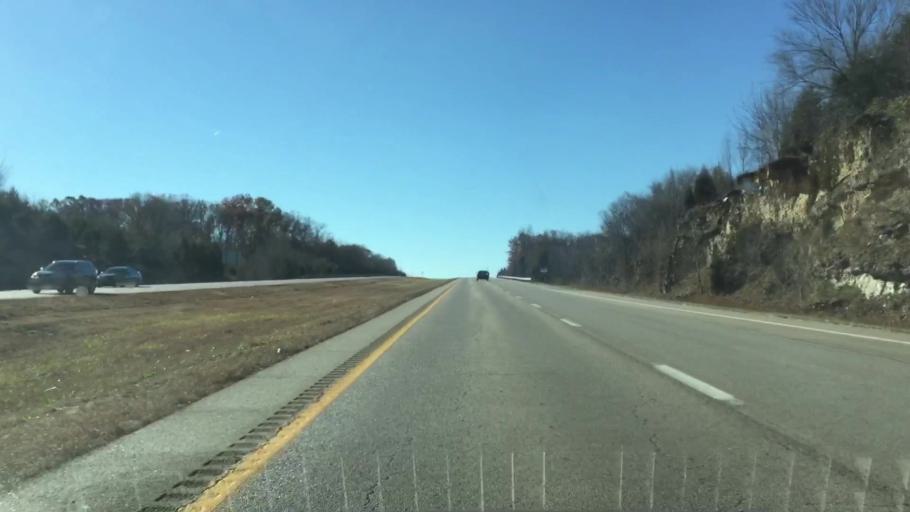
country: US
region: Missouri
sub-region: Cole County
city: Wardsville
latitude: 38.5009
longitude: -92.2672
